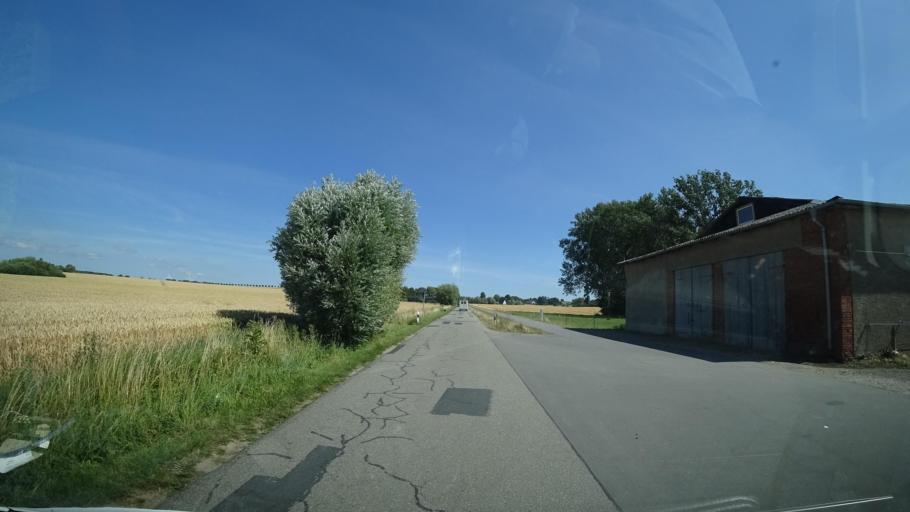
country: DE
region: Mecklenburg-Vorpommern
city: Blowatz
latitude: 54.0231
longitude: 11.5519
